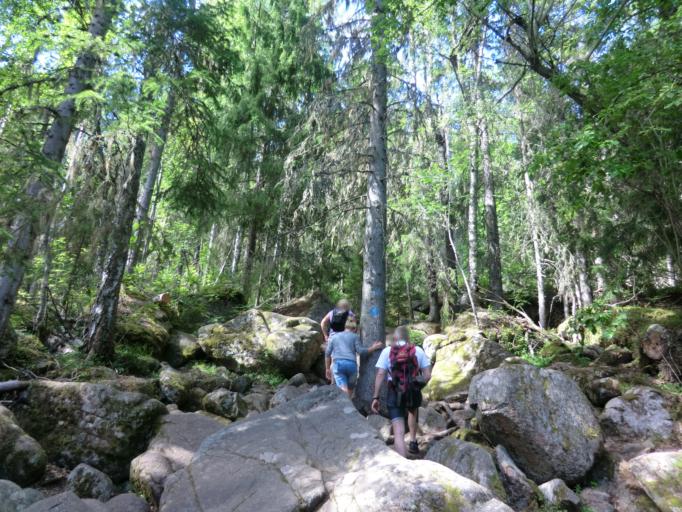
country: SE
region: Vaesternorrland
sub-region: Kramfors Kommun
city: Nordingra
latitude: 63.0723
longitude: 18.3528
